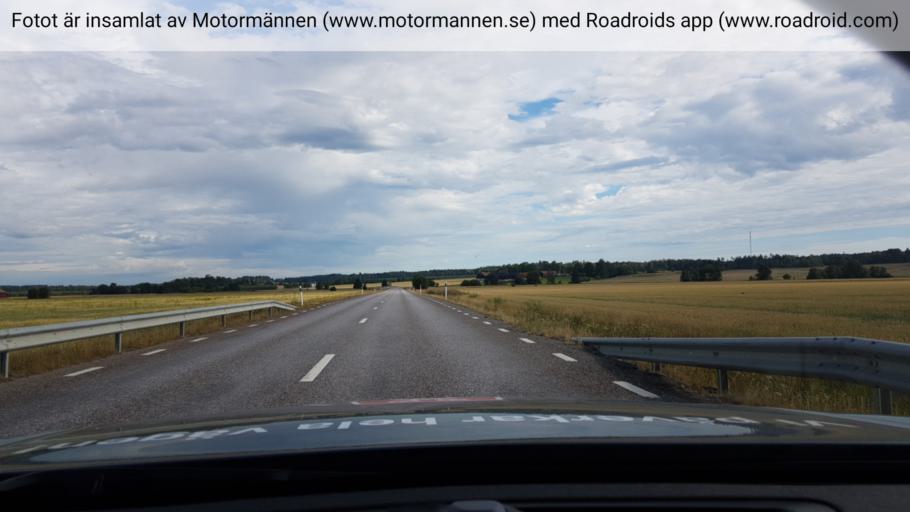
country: SE
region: Uppsala
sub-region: Heby Kommun
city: Morgongava
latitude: 59.8238
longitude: 16.9244
